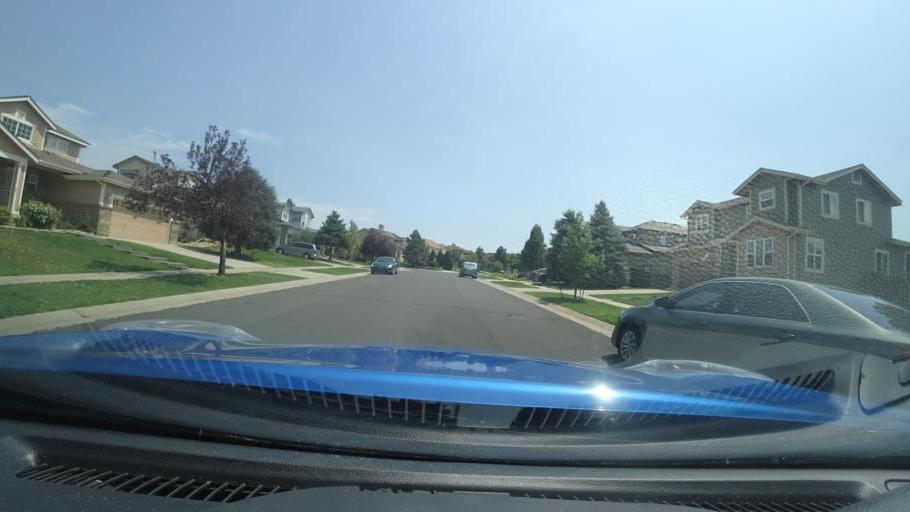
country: US
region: Colorado
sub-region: Adams County
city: Aurora
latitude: 39.6745
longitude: -104.7596
